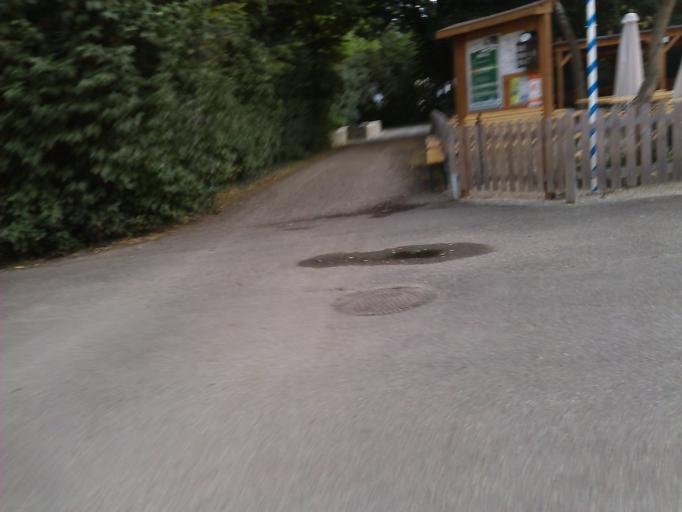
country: DE
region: Baden-Wuerttemberg
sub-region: Regierungsbezirk Stuttgart
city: Untereisesheim
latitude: 49.2292
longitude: 9.1983
